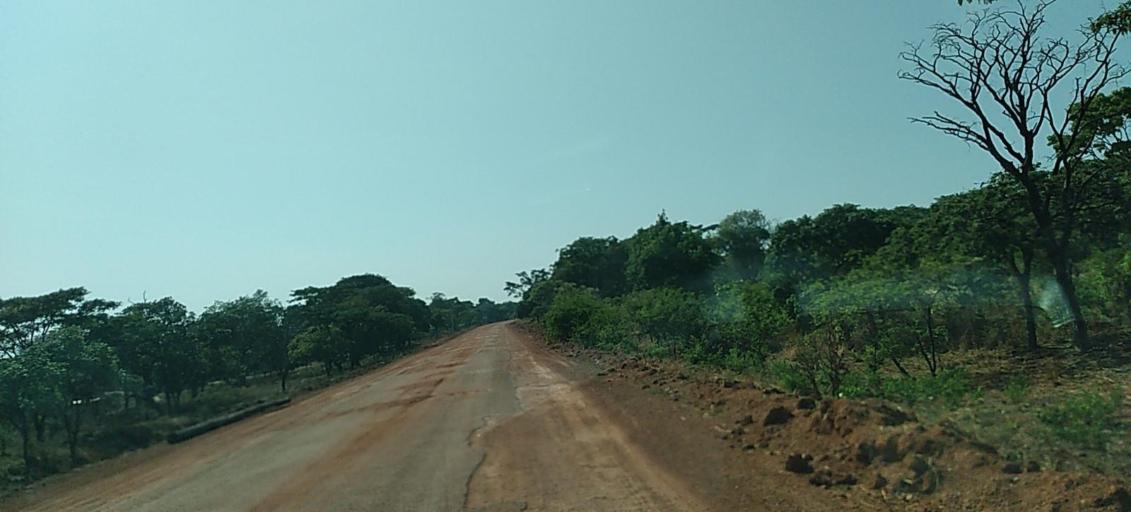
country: ZM
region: North-Western
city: Mwinilunga
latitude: -11.9189
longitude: 25.3134
